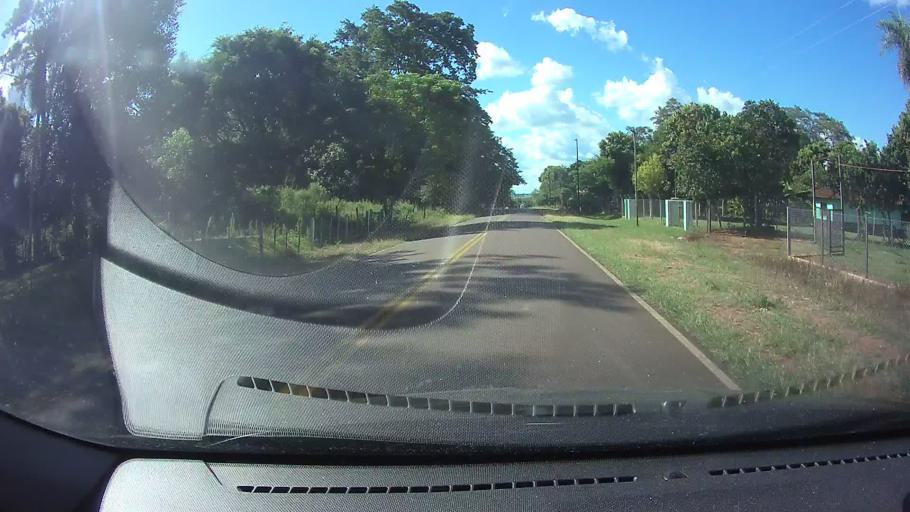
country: PY
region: Paraguari
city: Sapucai
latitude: -25.6546
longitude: -56.8611
